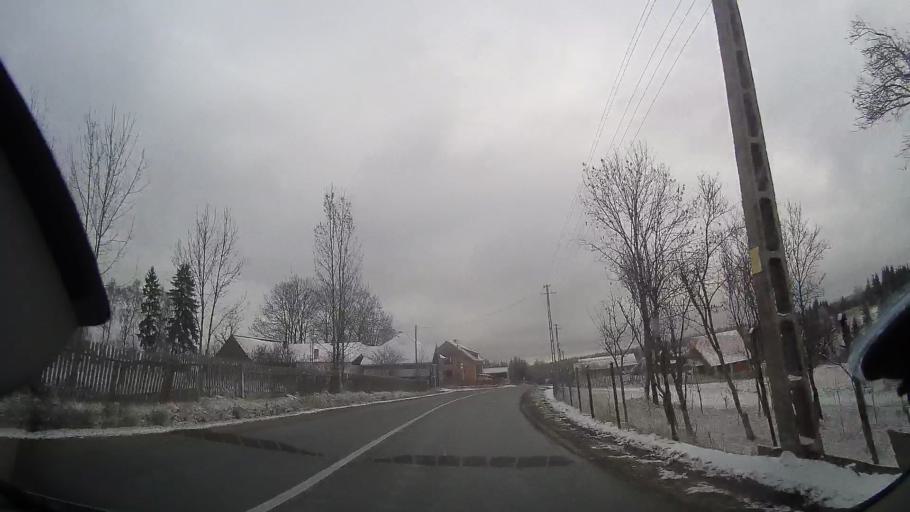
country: RO
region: Cluj
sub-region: Comuna Belis
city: Belis
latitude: 46.7077
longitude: 23.0383
